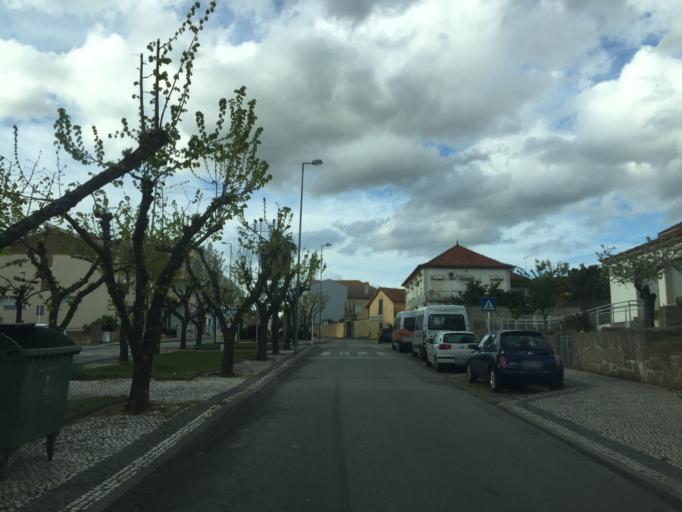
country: PT
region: Braganca
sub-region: Alfandega da Fe
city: Alfandega da Fe
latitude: 41.3397
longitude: -6.9628
